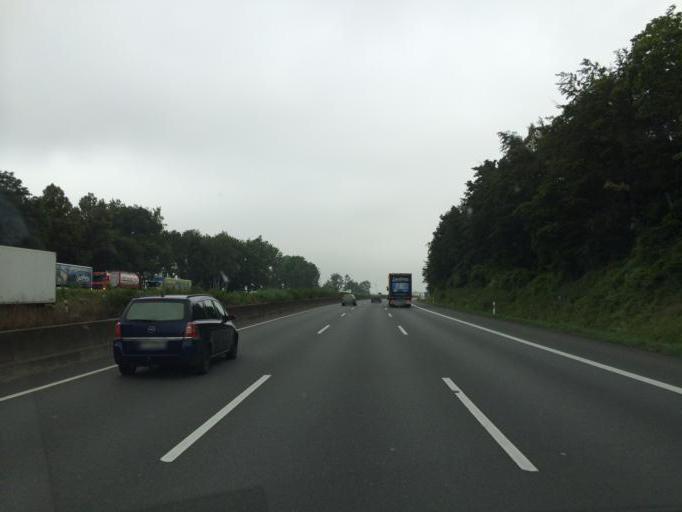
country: DE
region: North Rhine-Westphalia
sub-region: Regierungsbezirk Munster
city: Beckum
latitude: 51.7227
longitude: 7.9800
